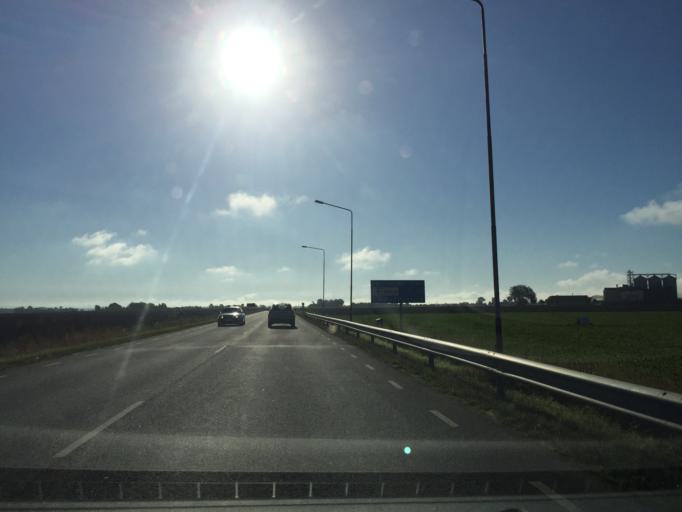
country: SE
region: Skane
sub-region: Lunds Kommun
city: Lund
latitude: 55.6761
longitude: 13.1852
